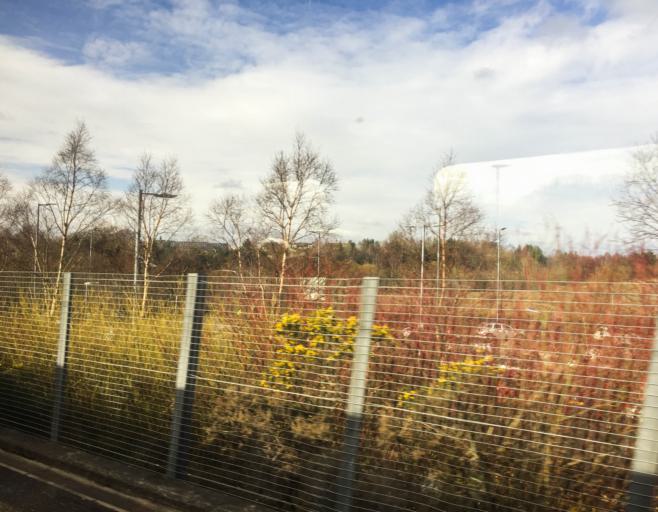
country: GB
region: Scotland
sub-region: North Lanarkshire
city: Chryston
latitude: 55.8856
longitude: -4.0790
